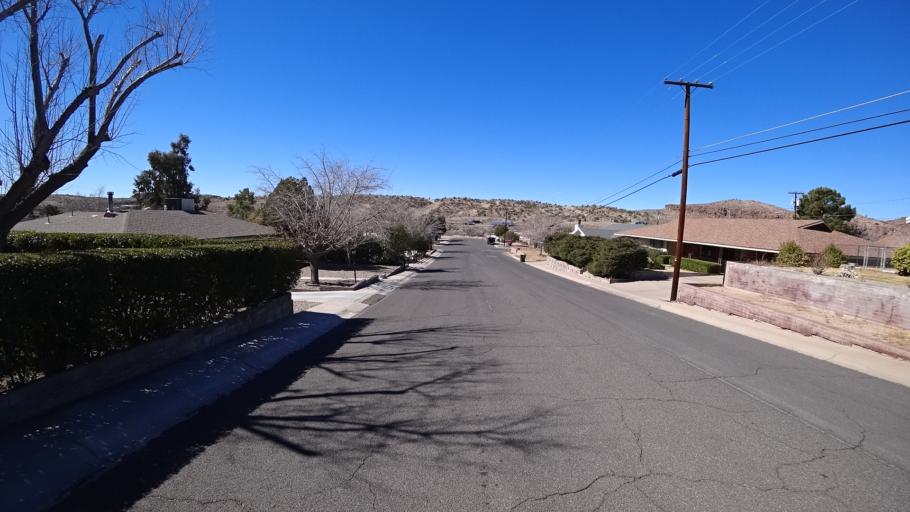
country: US
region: Arizona
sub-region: Mohave County
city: Kingman
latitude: 35.1975
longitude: -114.0635
